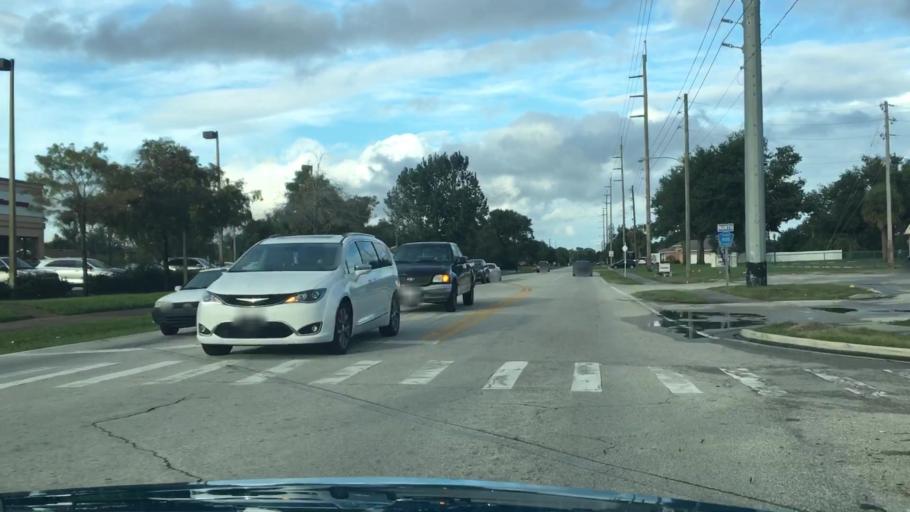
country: US
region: Florida
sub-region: Volusia County
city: Deltona
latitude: 28.8839
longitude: -81.2398
